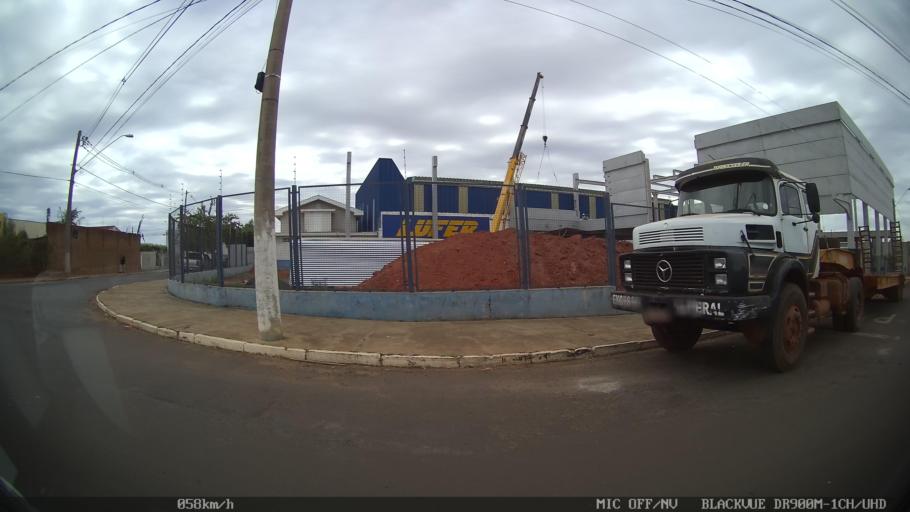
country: BR
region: Sao Paulo
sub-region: Bady Bassitt
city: Bady Bassitt
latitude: -20.8150
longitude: -49.4936
